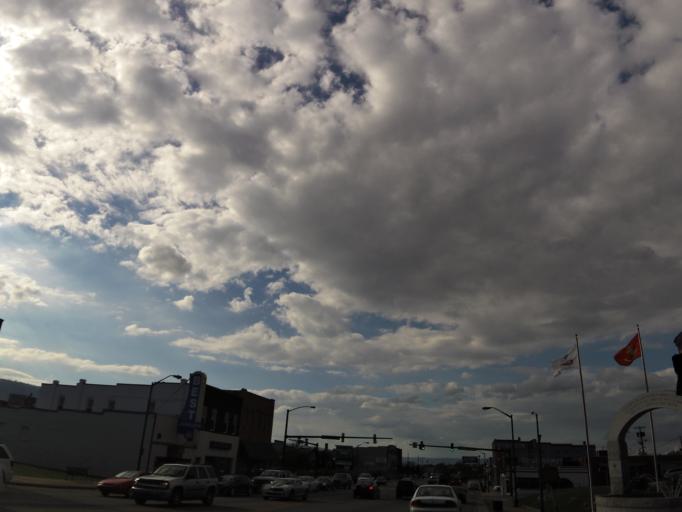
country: US
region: Georgia
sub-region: Walker County
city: Rossville
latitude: 34.9836
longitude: -85.2864
